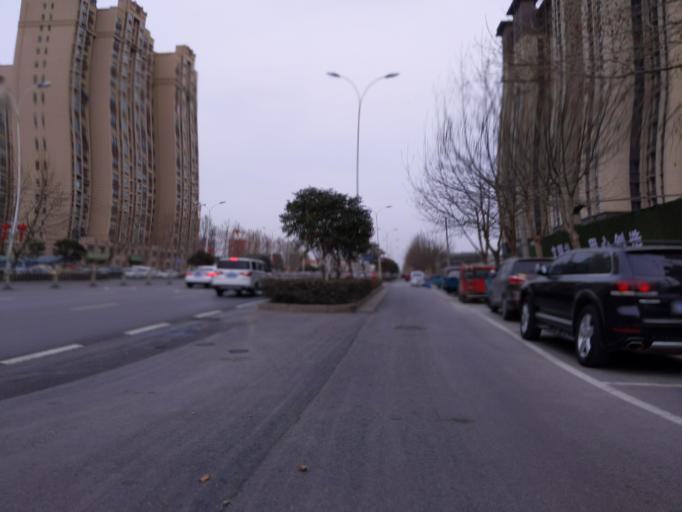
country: CN
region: Henan Sheng
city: Zhongyuanlu
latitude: 35.7576
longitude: 115.0747
